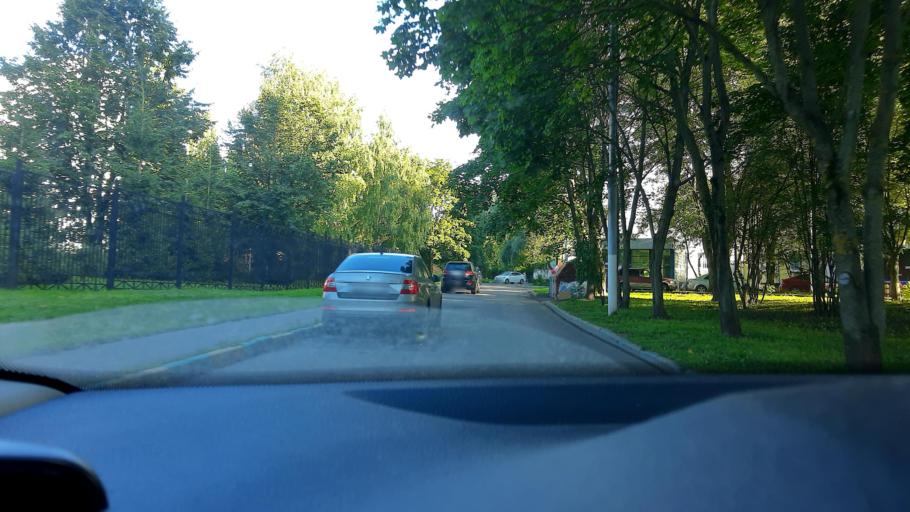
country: RU
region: Moscow
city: Khimki
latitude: 55.8606
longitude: 37.4112
